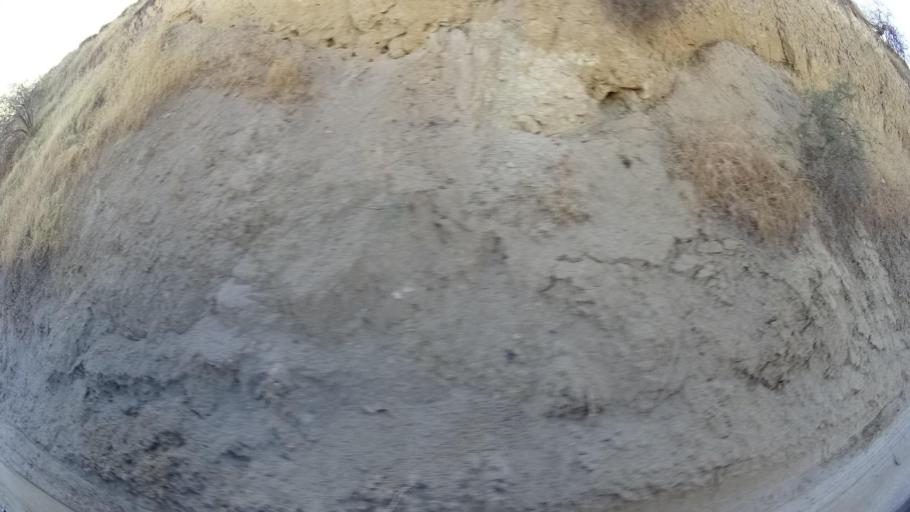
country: US
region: California
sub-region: Kern County
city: Oildale
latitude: 35.4973
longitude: -118.8953
